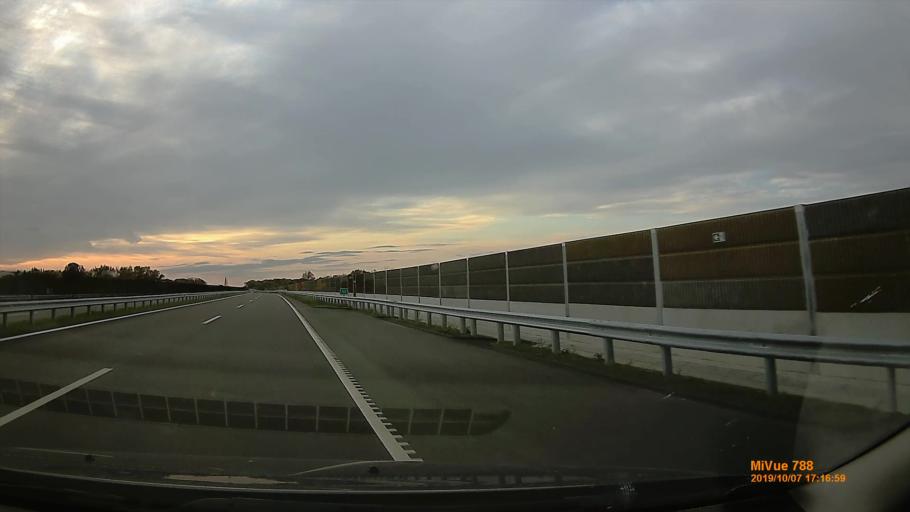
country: HU
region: Jasz-Nagykun-Szolnok
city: Kunszentmarton
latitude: 46.8620
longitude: 20.2985
